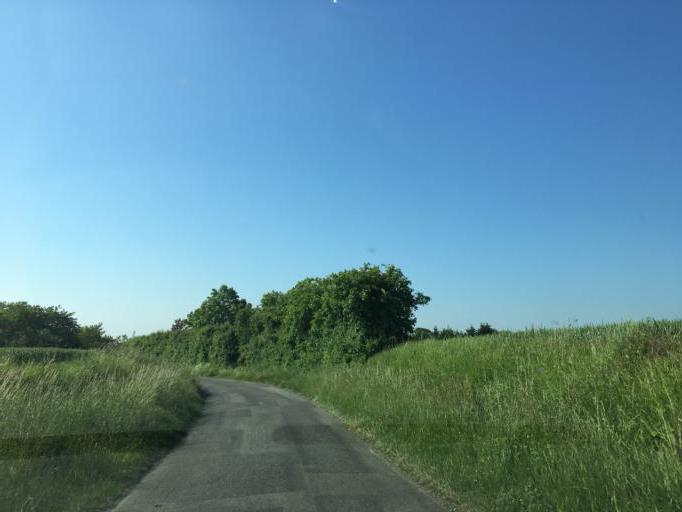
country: FR
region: Poitou-Charentes
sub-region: Departement des Deux-Sevres
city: Beauvoir-sur-Niort
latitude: 46.0785
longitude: -0.5087
